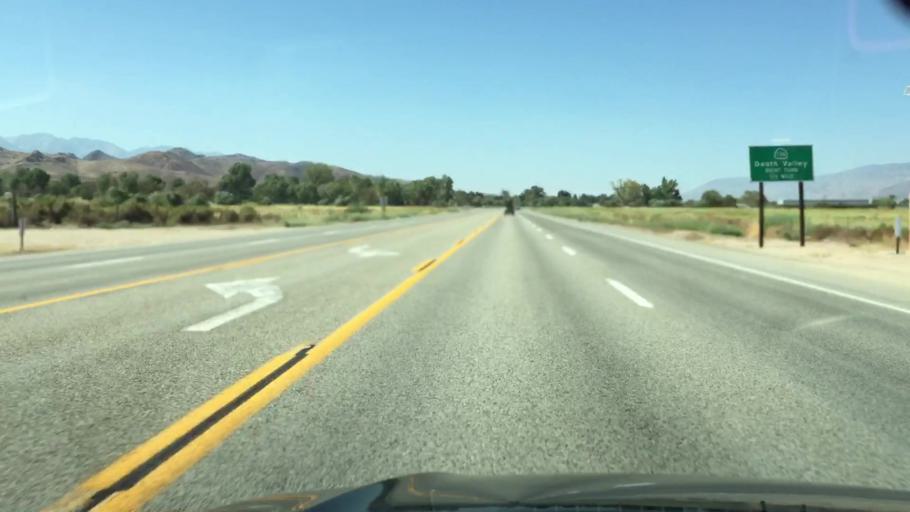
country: US
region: California
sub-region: Inyo County
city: Lone Pine
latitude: 36.5720
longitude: -118.0553
